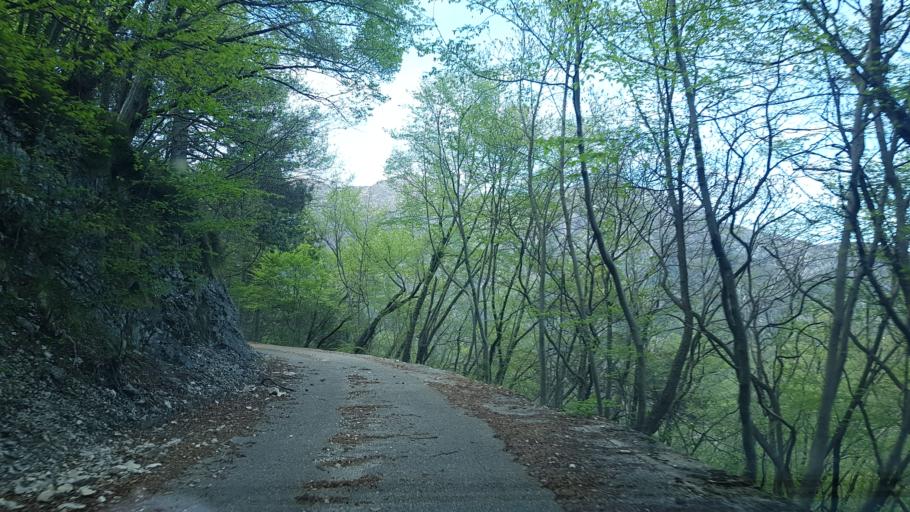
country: IT
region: Friuli Venezia Giulia
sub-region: Provincia di Udine
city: Cavazzo Carnico
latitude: 46.3119
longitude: 13.0237
